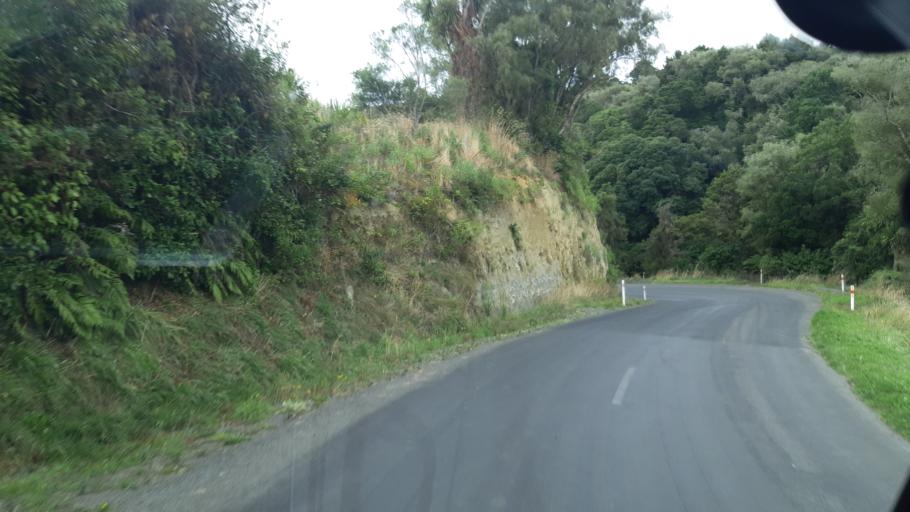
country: NZ
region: Manawatu-Wanganui
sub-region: Ruapehu District
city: Waiouru
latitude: -39.5529
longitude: 175.6395
